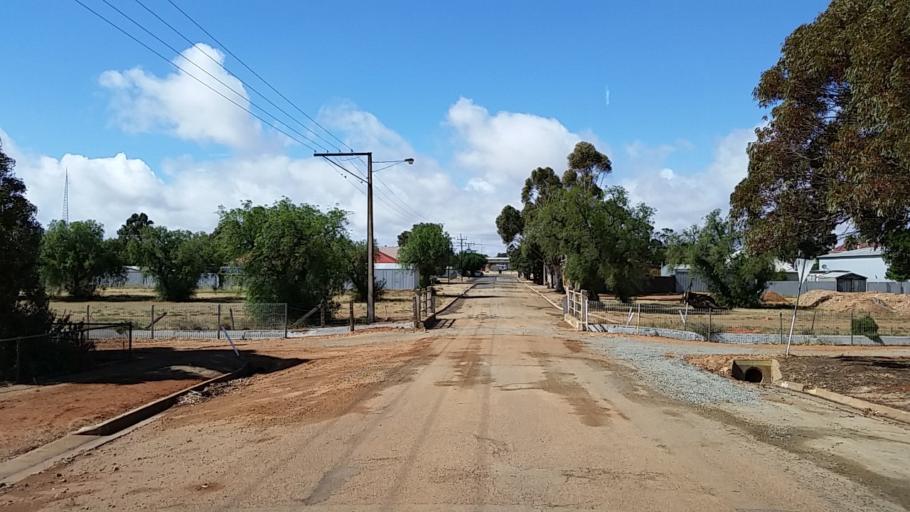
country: AU
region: South Australia
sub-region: Peterborough
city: Peterborough
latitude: -32.9710
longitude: 138.8361
